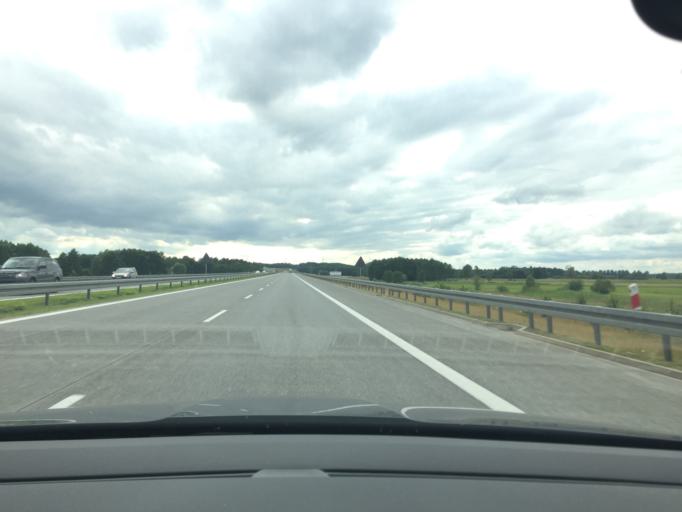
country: PL
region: Lubusz
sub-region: Powiat miedzyrzecki
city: Brojce
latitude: 52.2972
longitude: 15.6918
